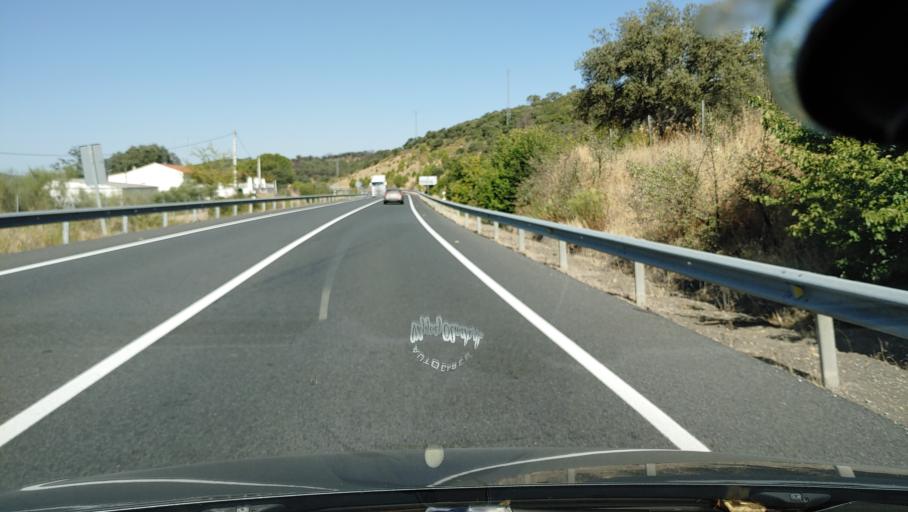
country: ES
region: Andalusia
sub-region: Province of Cordoba
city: Villaharta
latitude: 38.1289
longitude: -4.9090
